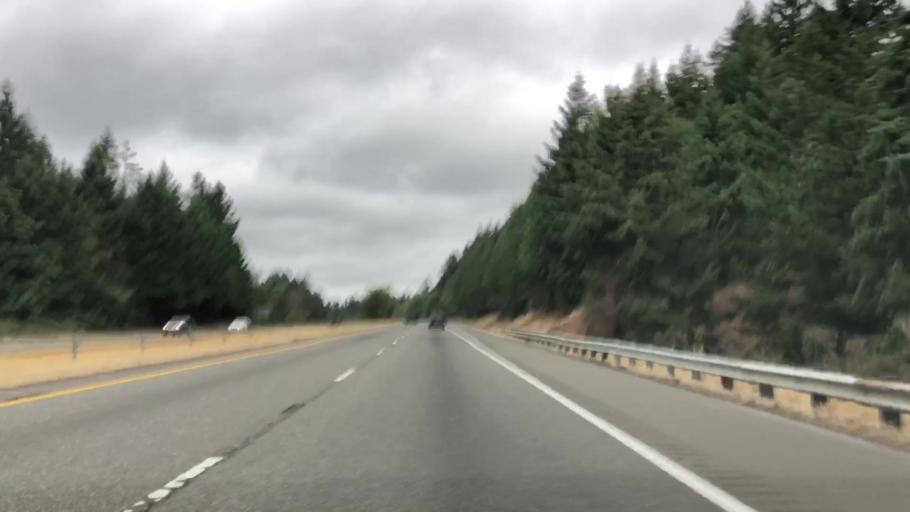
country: US
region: Washington
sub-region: Pierce County
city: Purdy
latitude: 47.3828
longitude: -122.6155
